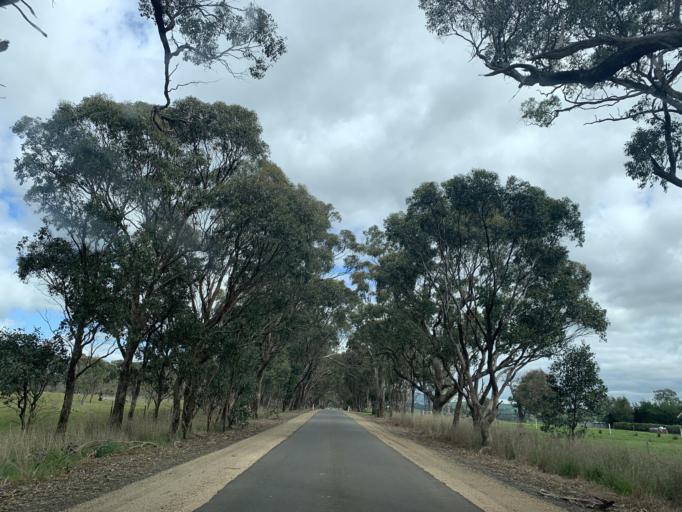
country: AU
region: Victoria
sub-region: Whittlesea
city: Whittlesea
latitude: -37.1577
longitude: 144.9223
